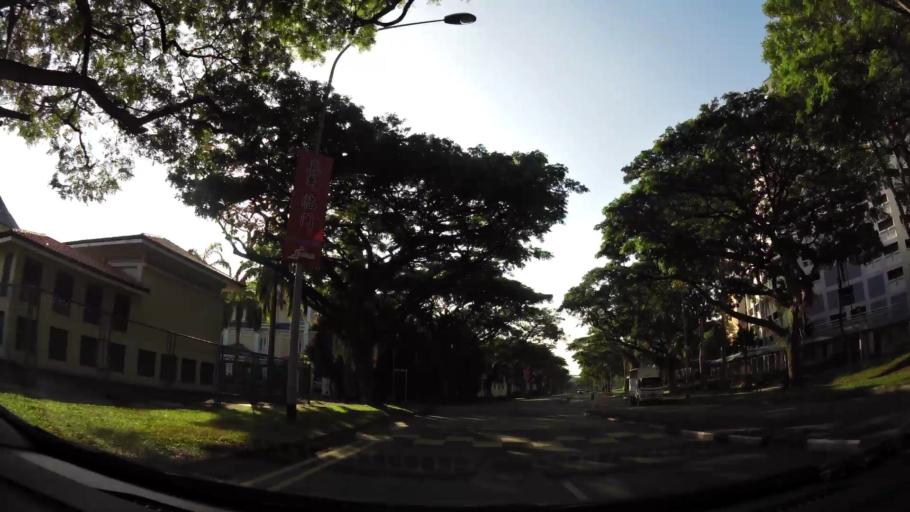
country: SG
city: Singapore
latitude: 1.3206
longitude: 103.9470
